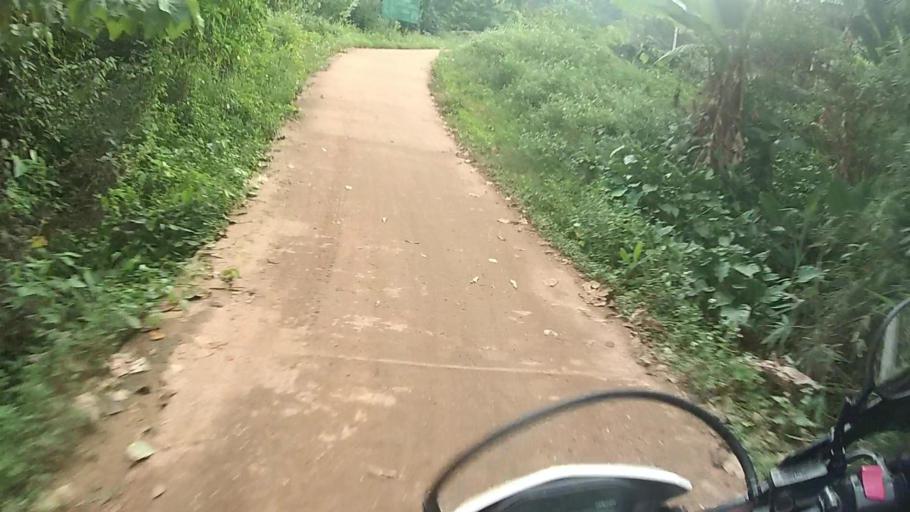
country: TH
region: Lampang
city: Wang Nuea
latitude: 19.0893
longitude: 99.4930
